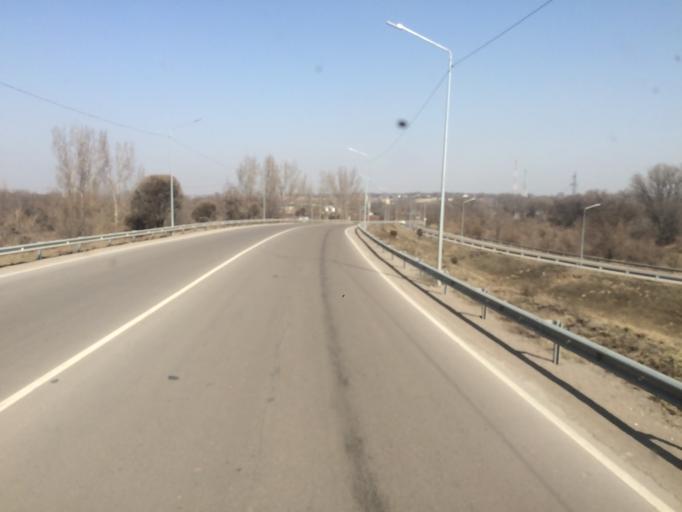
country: KZ
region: Almaty Oblysy
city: Burunday
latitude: 43.2197
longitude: 76.6493
